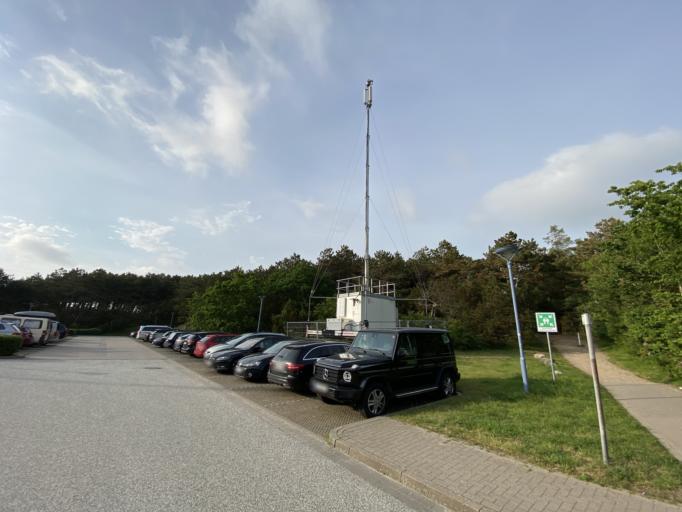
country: DE
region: Schleswig-Holstein
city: Sankt Peter-Ording
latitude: 54.3161
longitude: 8.6050
